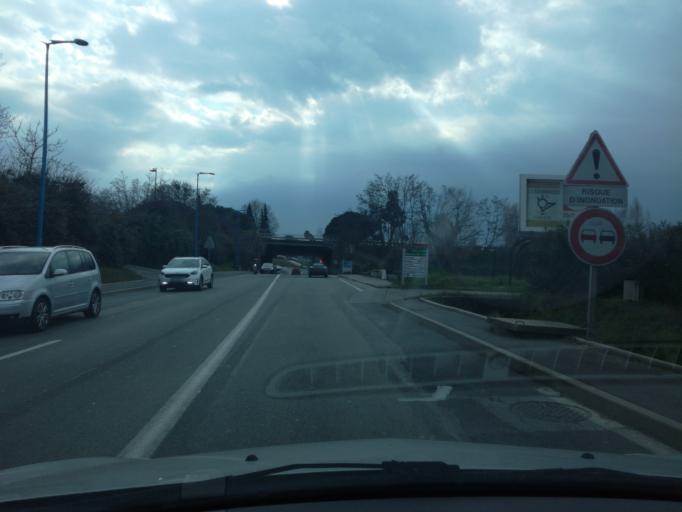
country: FR
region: Provence-Alpes-Cote d'Azur
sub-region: Departement des Alpes-Maritimes
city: Mandelieu-la-Napoule
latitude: 43.5591
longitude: 6.9513
